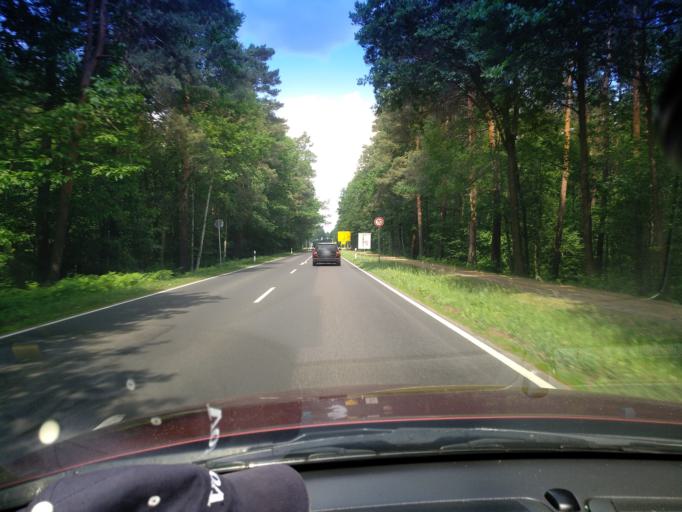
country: DE
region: Saxony
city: Niesky
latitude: 51.2914
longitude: 14.8097
